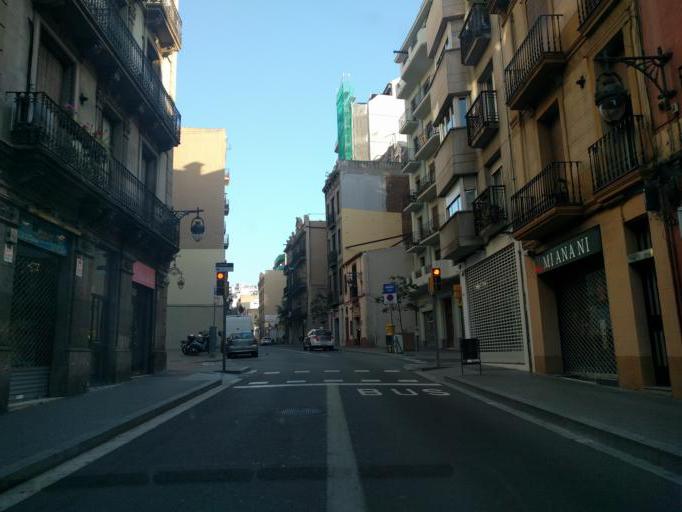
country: ES
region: Catalonia
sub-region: Provincia de Barcelona
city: Gracia
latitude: 41.4037
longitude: 2.1520
